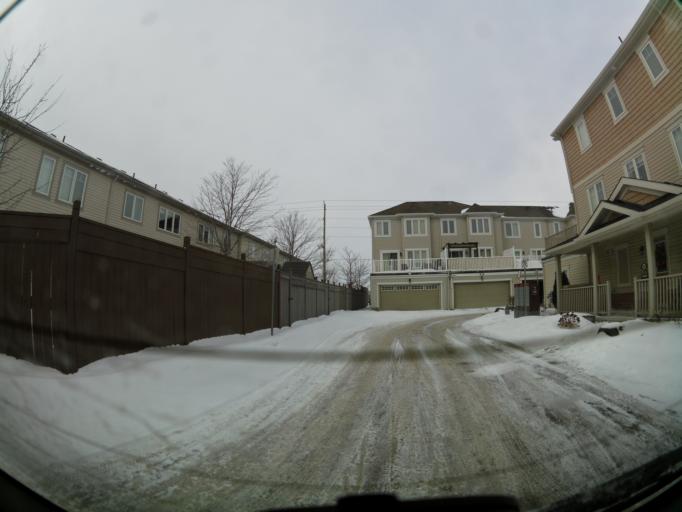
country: CA
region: Ontario
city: Bells Corners
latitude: 45.2898
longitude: -75.9177
